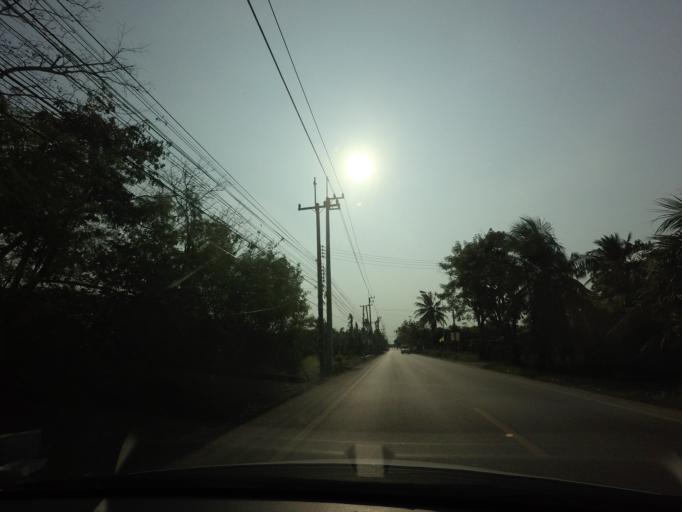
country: TH
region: Nakhon Pathom
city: Sam Phran
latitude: 13.6950
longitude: 100.2243
